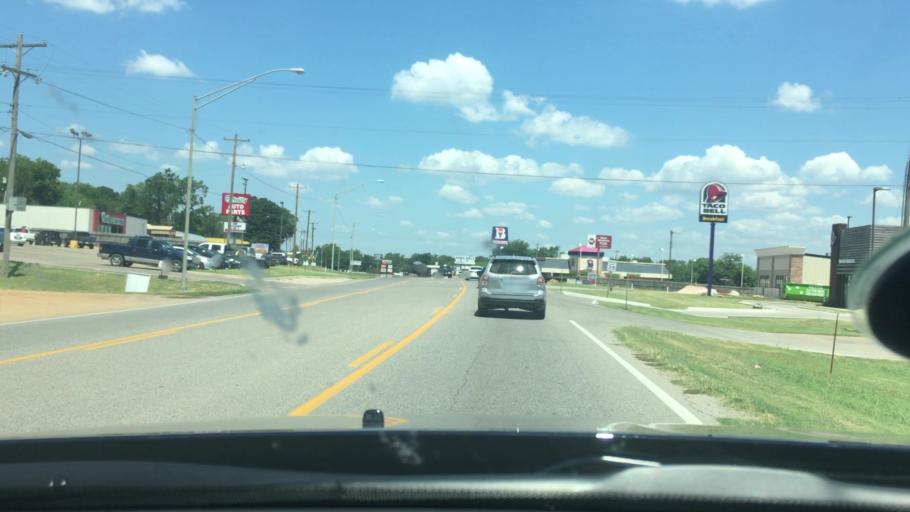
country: US
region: Oklahoma
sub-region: Marshall County
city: Madill
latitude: 34.0789
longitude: -96.7638
